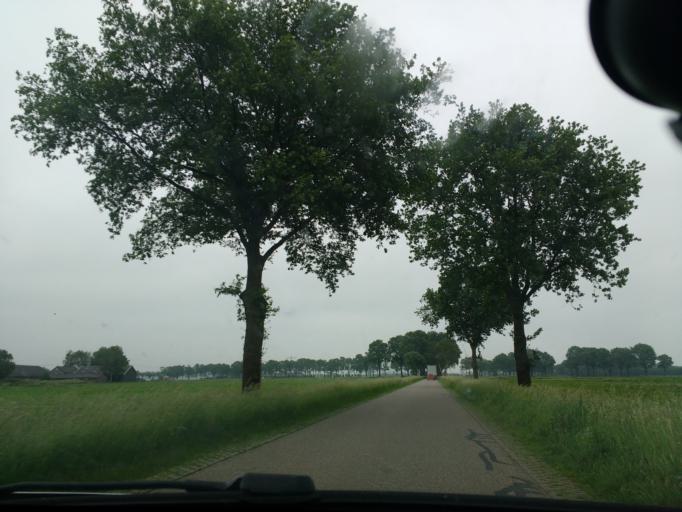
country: NL
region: Utrecht
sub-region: Gemeente Rhenen
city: Rhenen
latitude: 51.9927
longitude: 5.5837
